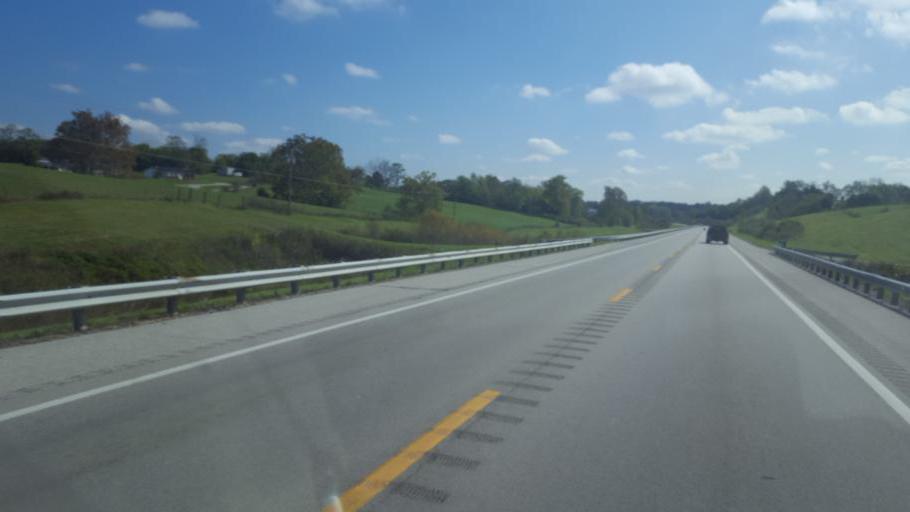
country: US
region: Kentucky
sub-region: Mason County
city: Maysville
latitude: 38.5888
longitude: -83.7074
